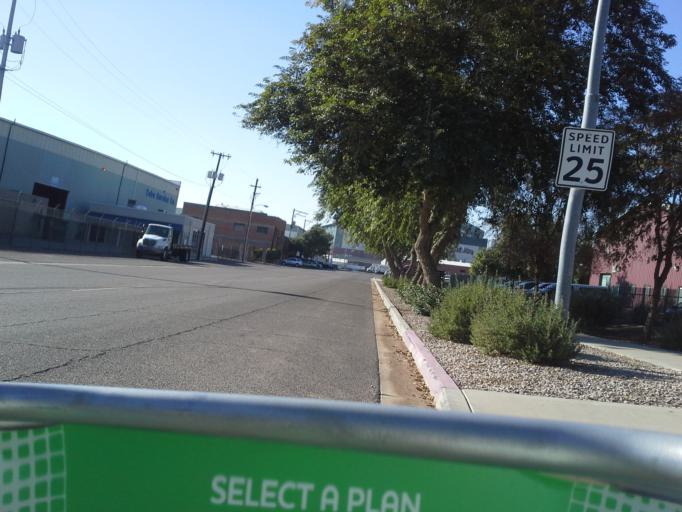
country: US
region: Arizona
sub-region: Maricopa County
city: Phoenix
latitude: 33.4451
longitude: -112.0578
